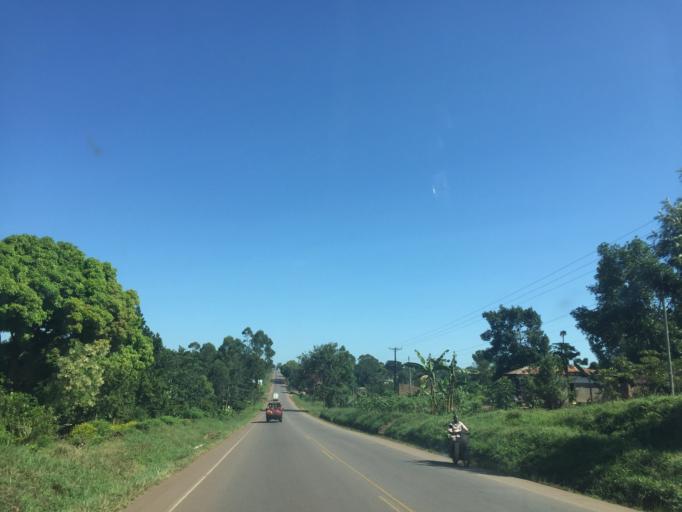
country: UG
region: Central Region
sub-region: Luwero District
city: Wobulenzi
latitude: 0.7426
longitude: 32.5167
